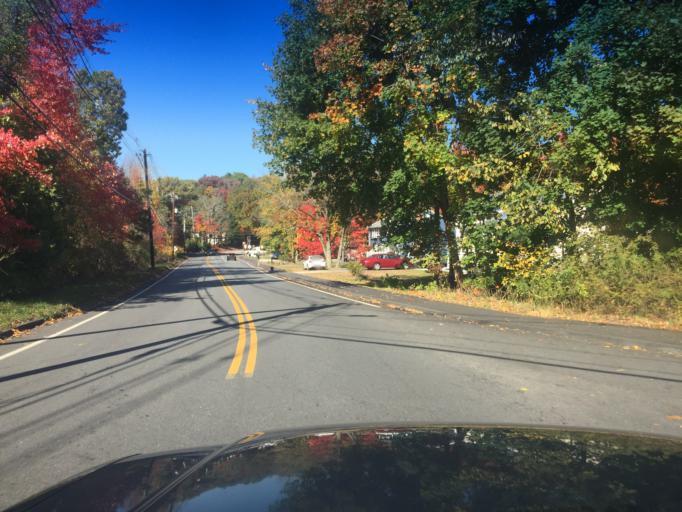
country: US
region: Massachusetts
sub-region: Middlesex County
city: Hudson
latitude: 42.3861
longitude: -71.5489
